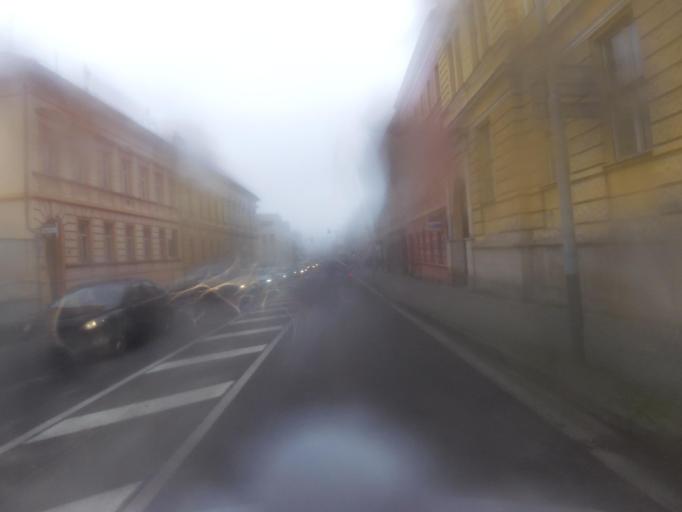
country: CZ
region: Ustecky
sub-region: Okres Louny
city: Louny
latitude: 50.3554
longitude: 13.7971
